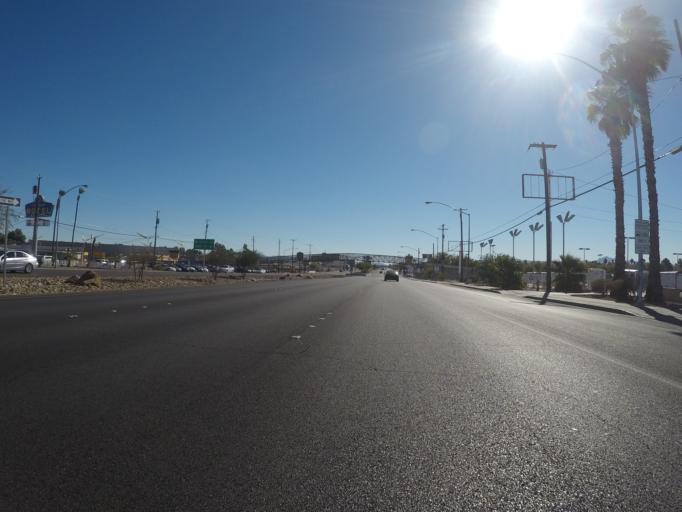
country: US
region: Nevada
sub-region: Clark County
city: Winchester
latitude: 36.1426
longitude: -115.0982
